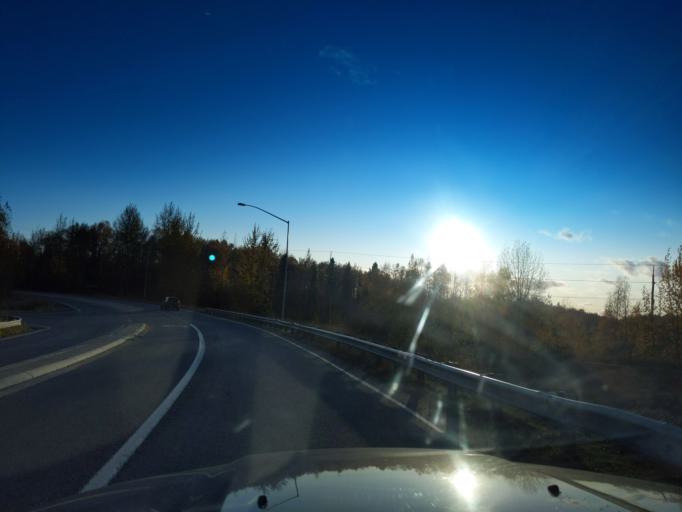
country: US
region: Alaska
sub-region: Anchorage Municipality
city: Anchorage
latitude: 61.1660
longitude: -149.9511
